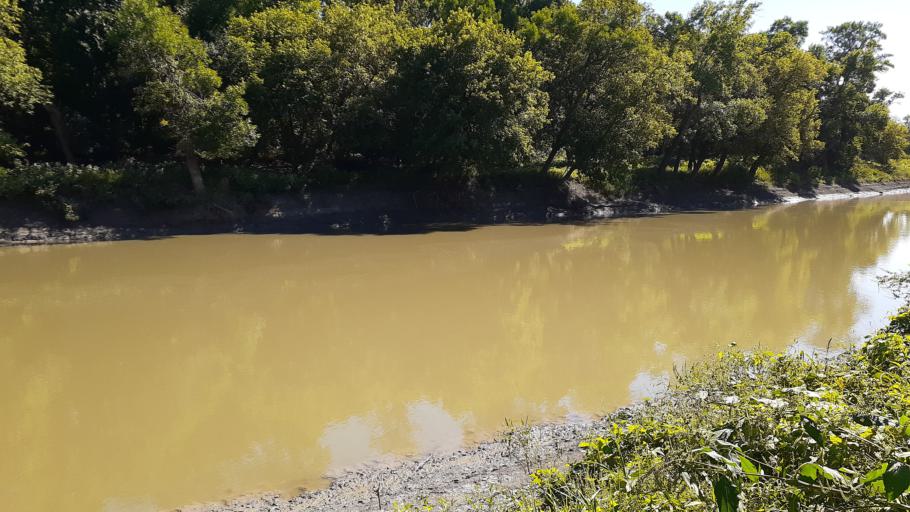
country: US
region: Minnesota
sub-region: Clay County
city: Oakport
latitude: 46.9158
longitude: -96.7590
